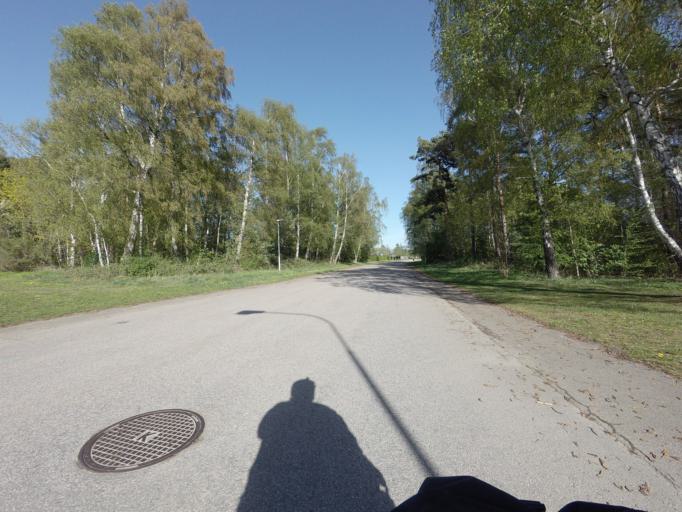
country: SE
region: Skane
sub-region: Landskrona
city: Asmundtorp
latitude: 55.8496
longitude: 12.9139
